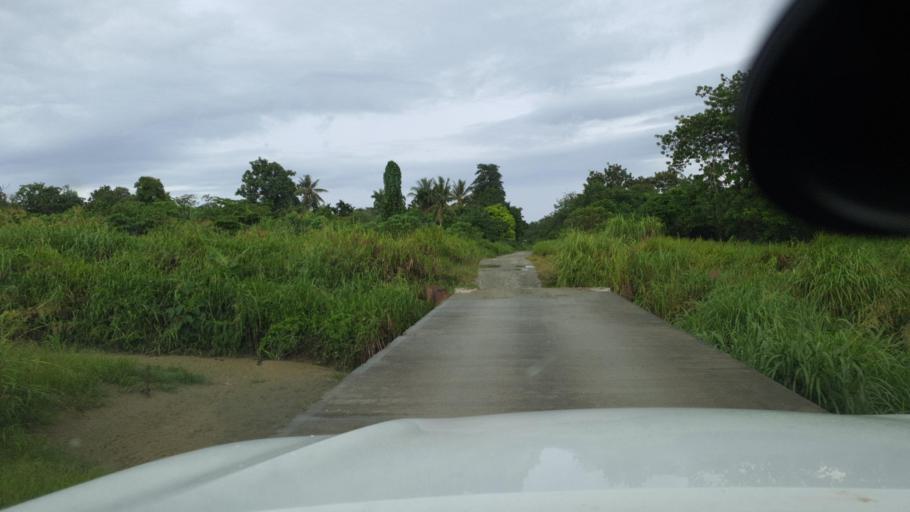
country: SB
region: Guadalcanal
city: Honiara
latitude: -9.4652
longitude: 160.3605
